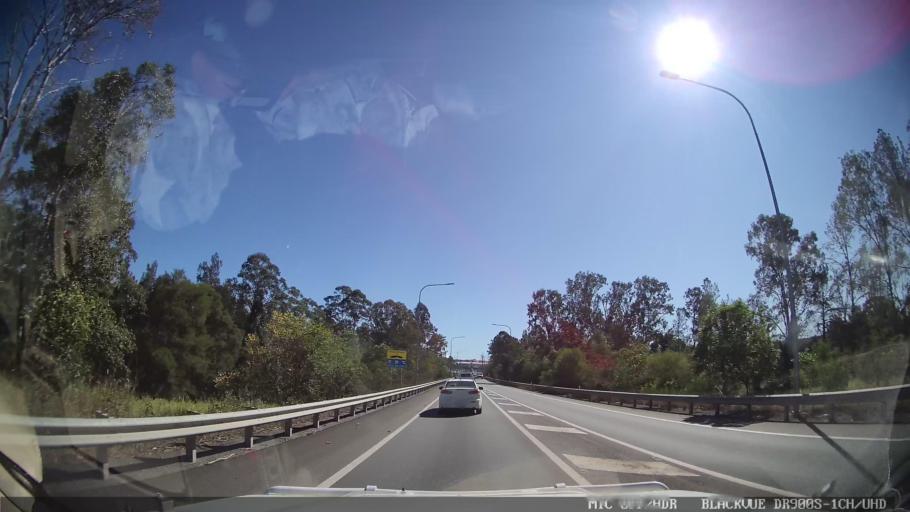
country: AU
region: Queensland
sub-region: Gympie Regional Council
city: Monkland
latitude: -26.2342
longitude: 152.6983
